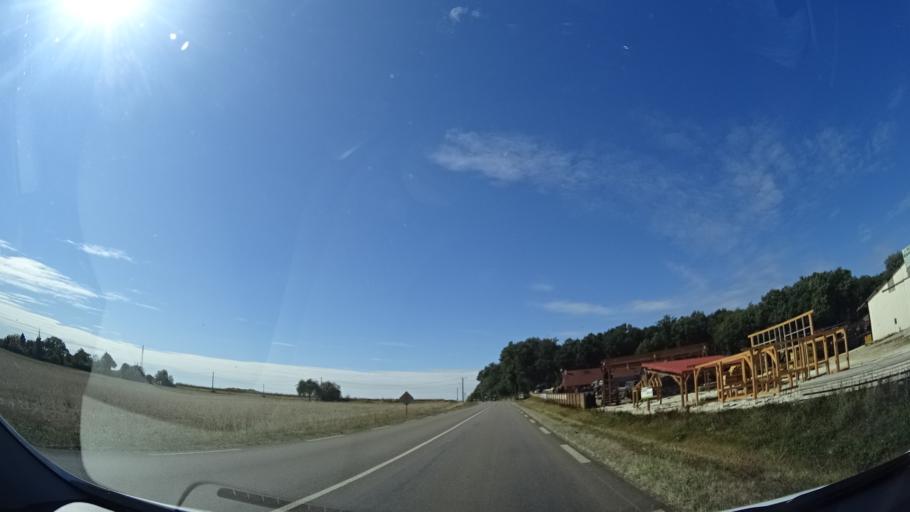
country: FR
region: Bourgogne
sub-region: Departement de l'Yonne
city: Charny
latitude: 47.9401
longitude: 3.1460
